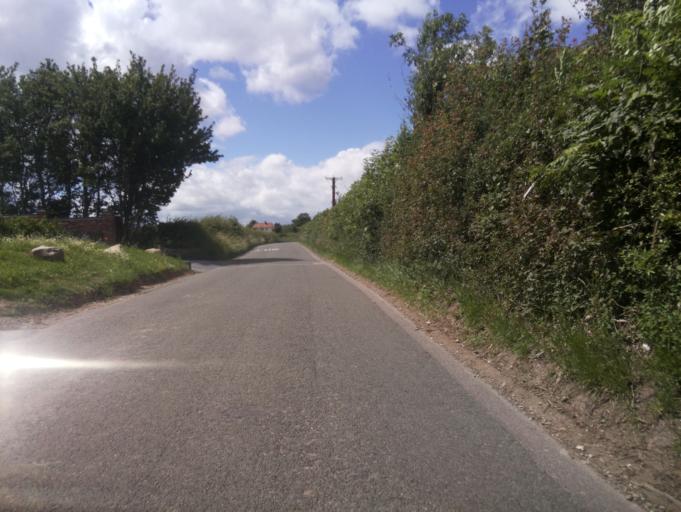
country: GB
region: England
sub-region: Nottinghamshire
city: Burton Joyce
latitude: 53.0034
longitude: -1.0703
